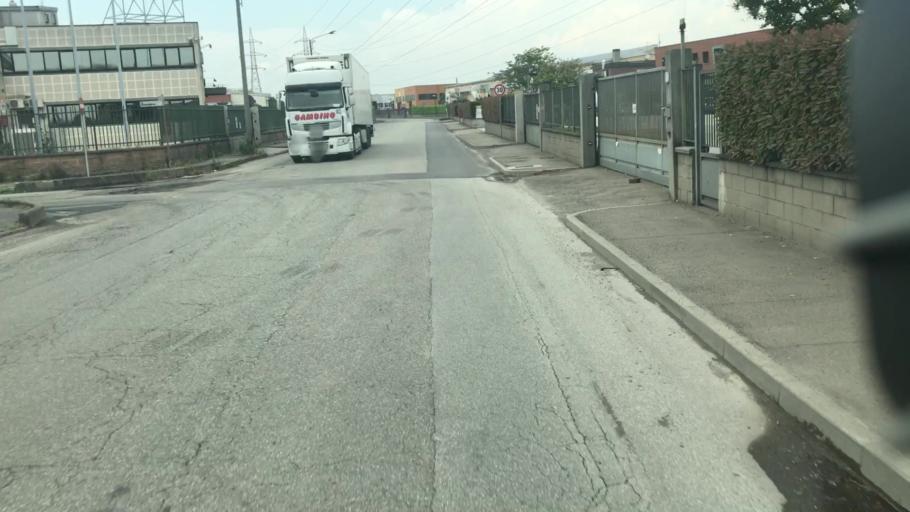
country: IT
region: Lombardy
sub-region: Citta metropolitana di Milano
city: Civesio
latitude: 45.3987
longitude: 9.2527
